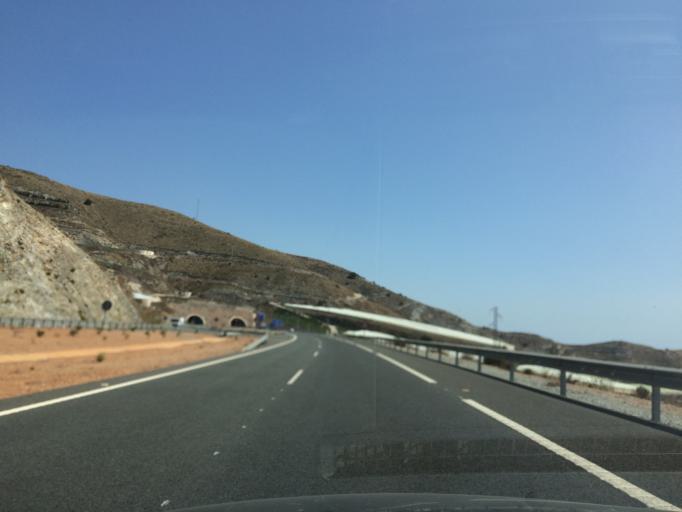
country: ES
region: Andalusia
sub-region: Provincia de Granada
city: Gualchos
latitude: 36.7155
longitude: -3.4497
